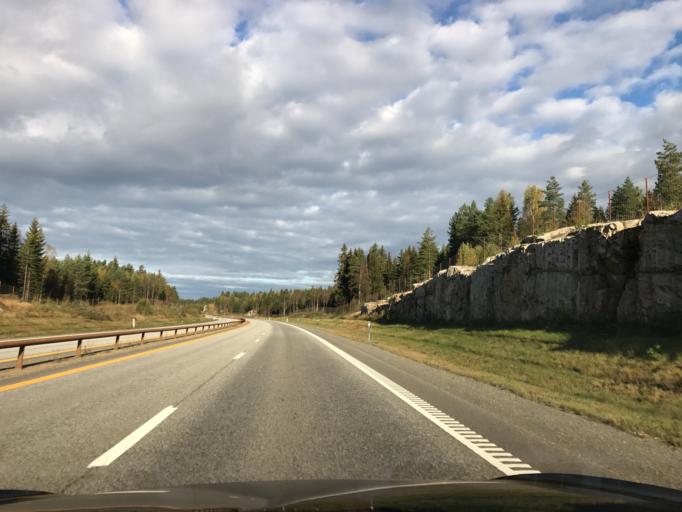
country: NO
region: Akershus
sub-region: Eidsvoll
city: Raholt
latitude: 60.2665
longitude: 11.1672
